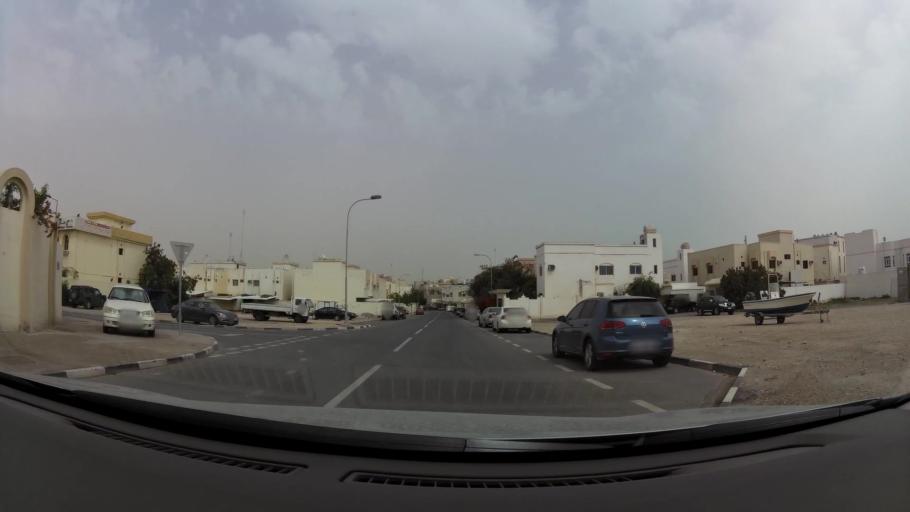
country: QA
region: Baladiyat ad Dawhah
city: Doha
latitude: 25.2619
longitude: 51.5491
